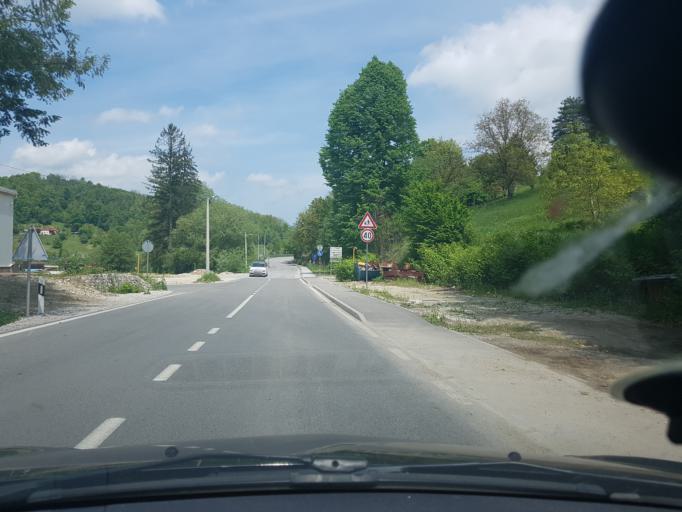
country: SI
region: Rogatec
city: Rogatec
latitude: 46.2205
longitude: 15.6945
